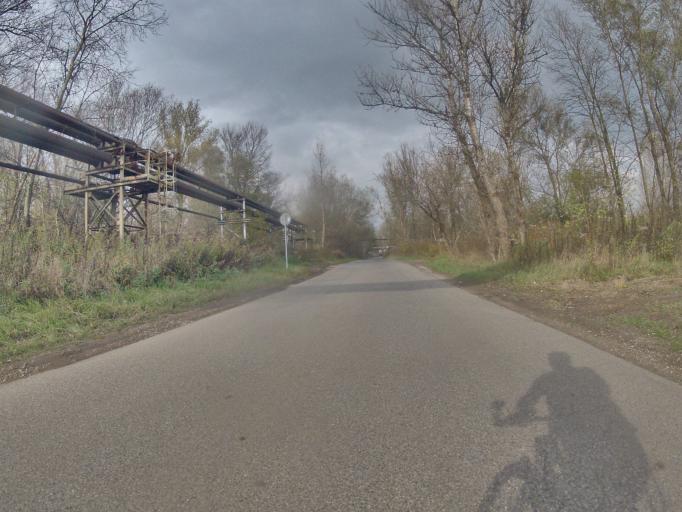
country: PL
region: Lesser Poland Voivodeship
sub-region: Powiat wielicki
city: Wegrzce Wielkie
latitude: 50.0628
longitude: 20.1025
